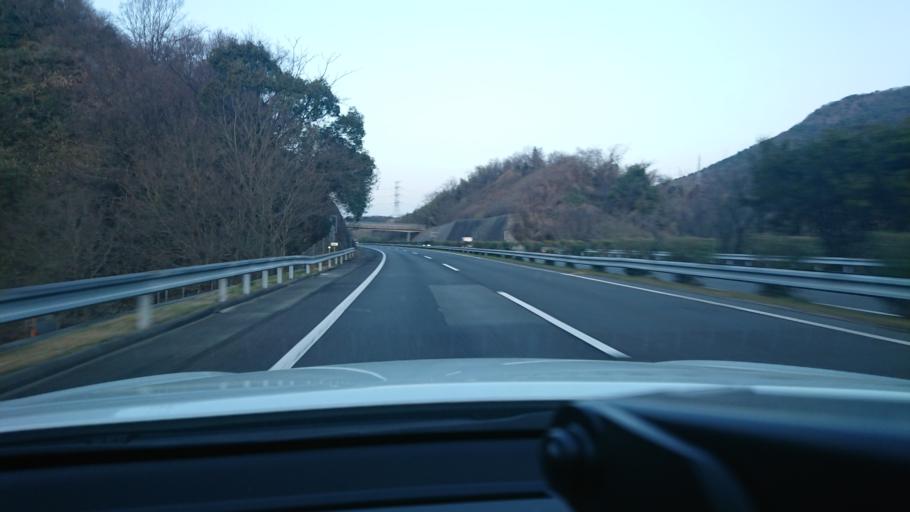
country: JP
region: Kagawa
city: Sakaidecho
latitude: 34.2776
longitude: 133.8966
